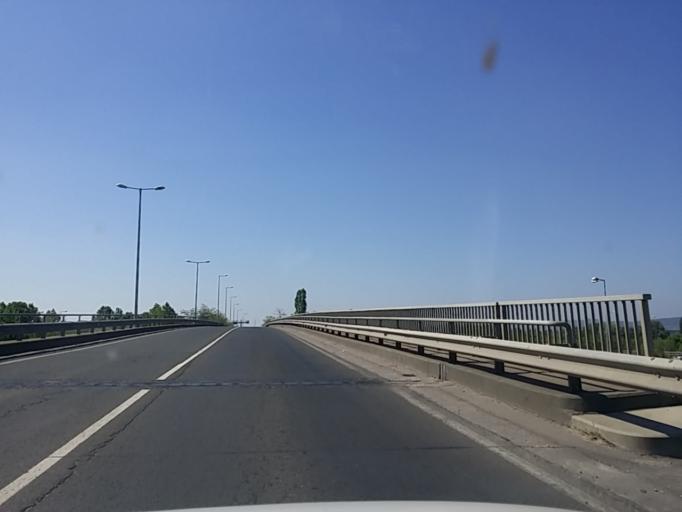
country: HU
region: Budapest
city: Budapest XV. keruelet
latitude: 47.5837
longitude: 19.1523
